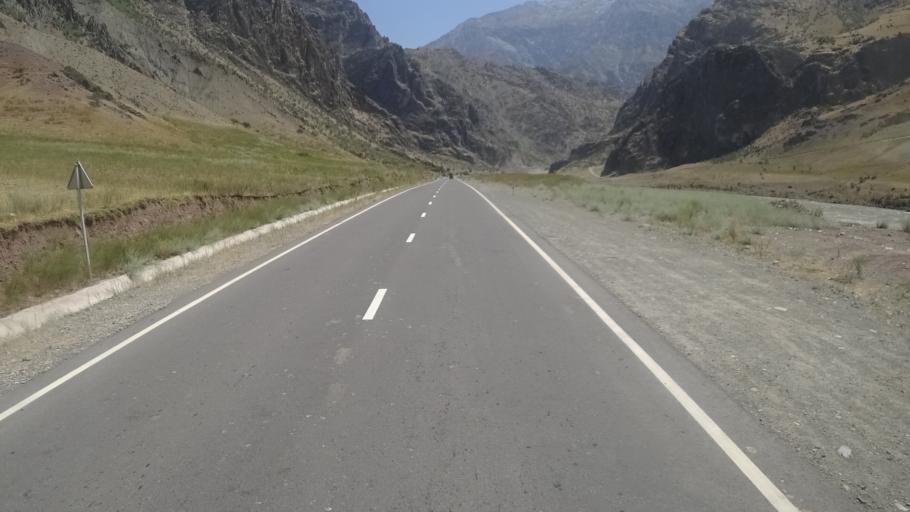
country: AF
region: Badakhshan
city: Deh Khwahan
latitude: 37.9421
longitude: 70.2336
